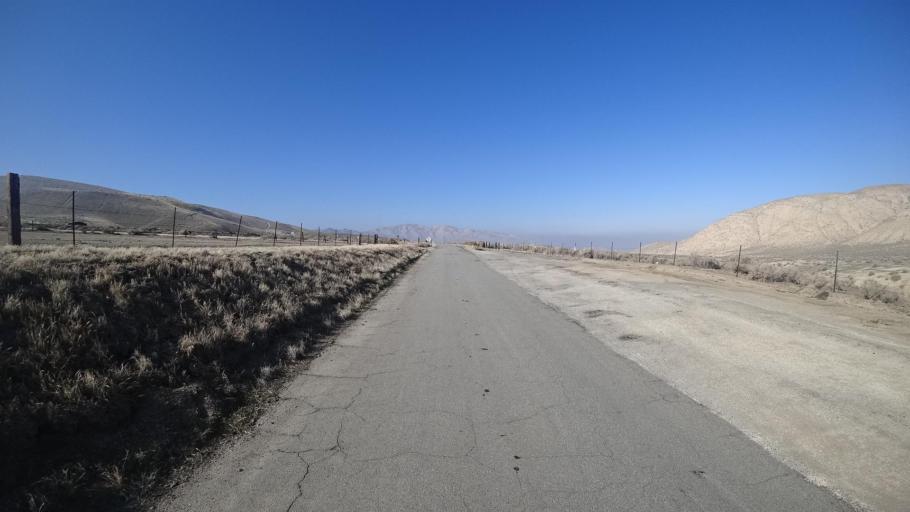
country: US
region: California
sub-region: Kern County
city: Maricopa
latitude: 35.0045
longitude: -119.4078
